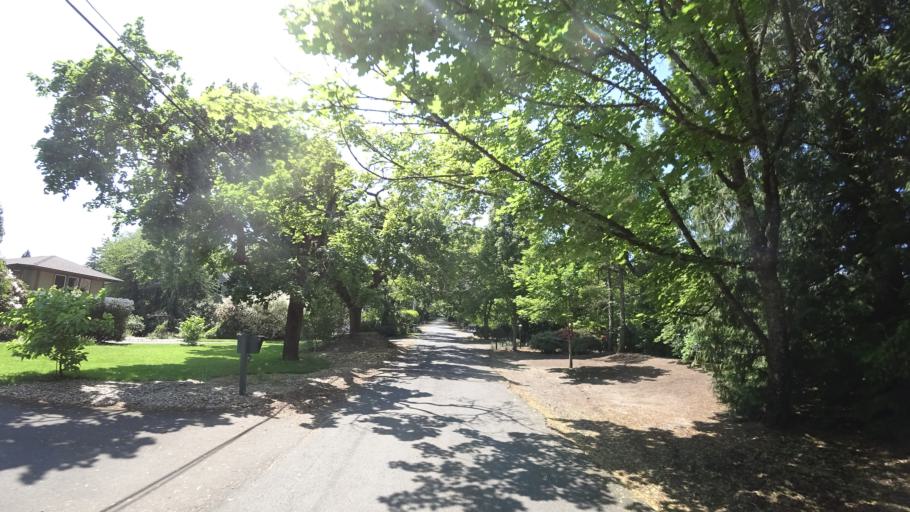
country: US
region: Oregon
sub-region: Clackamas County
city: Lake Oswego
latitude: 45.4343
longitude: -122.6911
